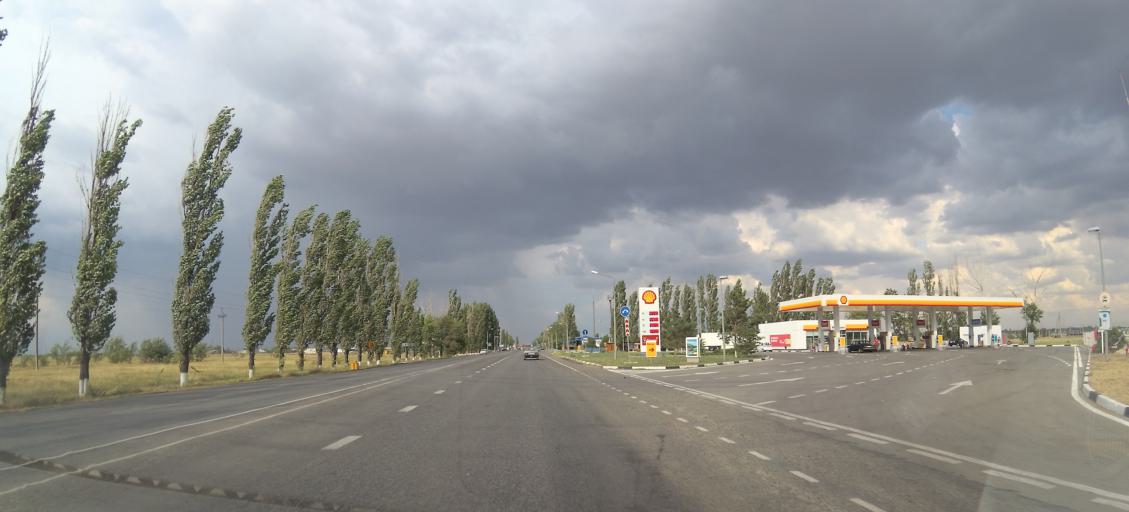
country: RU
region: Rostov
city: Zimovniki
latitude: 47.1402
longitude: 42.4347
